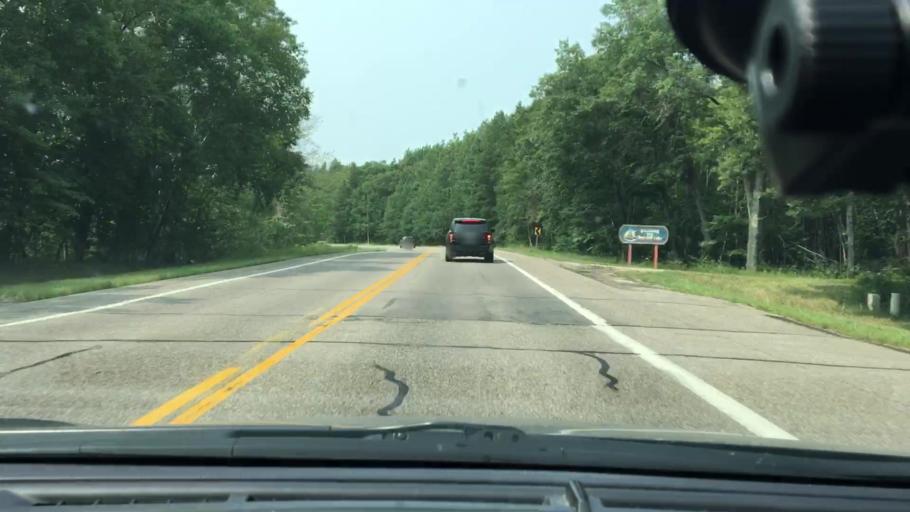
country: US
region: Minnesota
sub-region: Cass County
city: East Gull Lake
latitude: 46.3830
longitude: -94.3286
